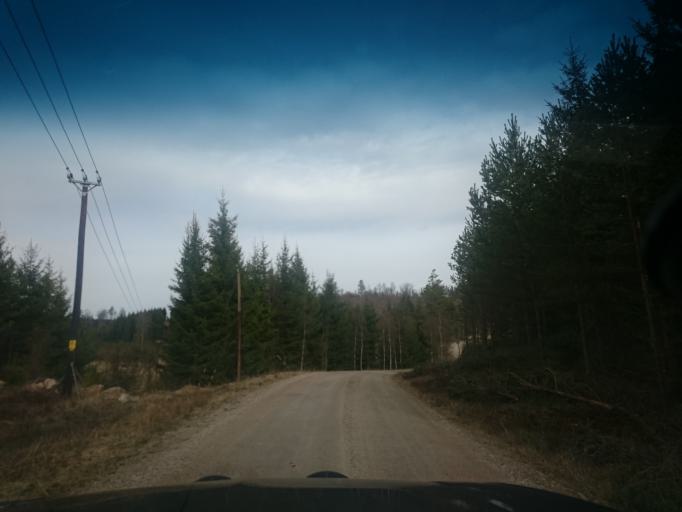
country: SE
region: Joenkoeping
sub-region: Vetlanda Kommun
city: Vetlanda
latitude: 57.3248
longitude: 15.1571
